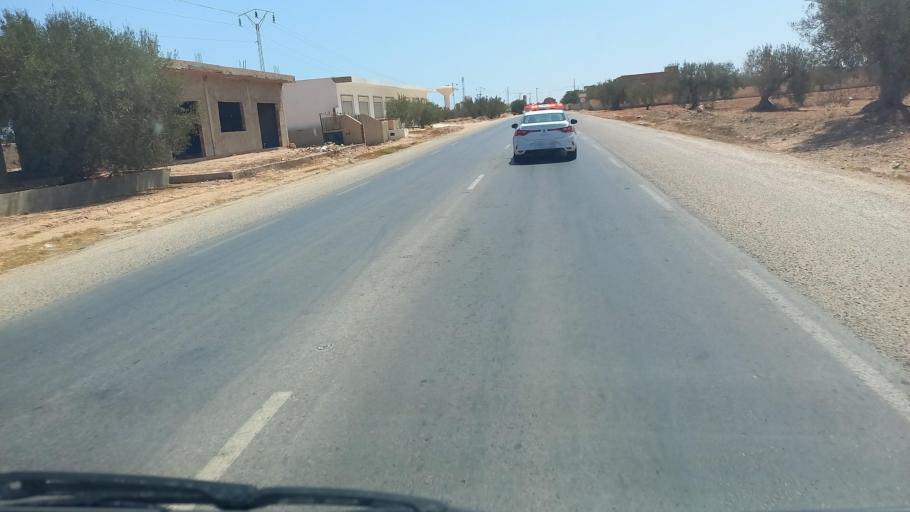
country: TN
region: Madanin
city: Zarzis
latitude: 33.5439
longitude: 11.0743
